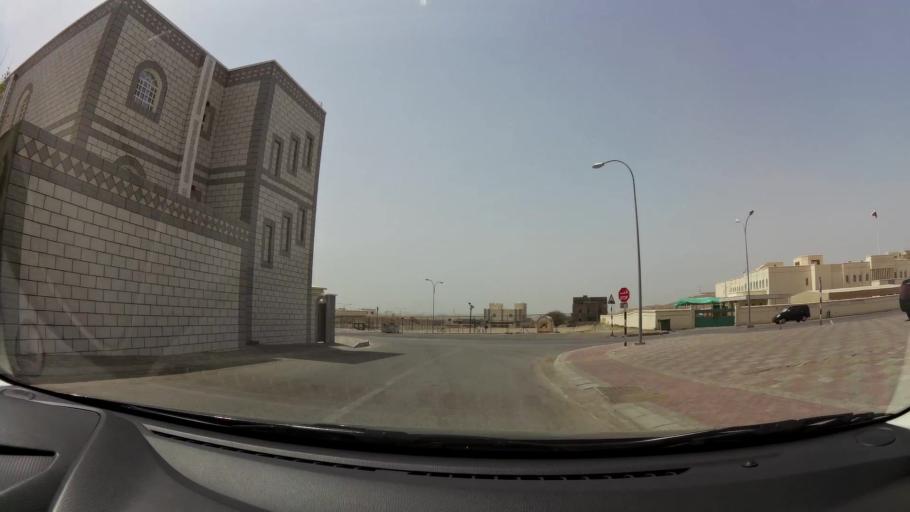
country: OM
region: Muhafazat Masqat
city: Bawshar
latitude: 23.5357
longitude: 58.3833
